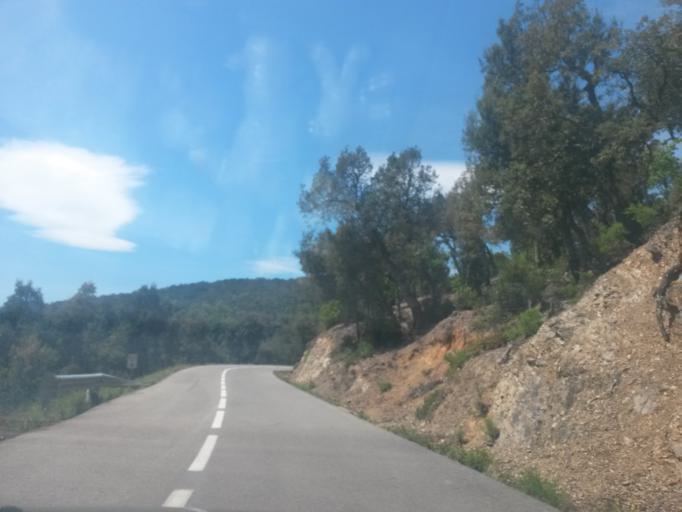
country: ES
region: Catalonia
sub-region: Provincia de Girona
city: Madremanya
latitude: 41.9374
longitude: 2.9298
